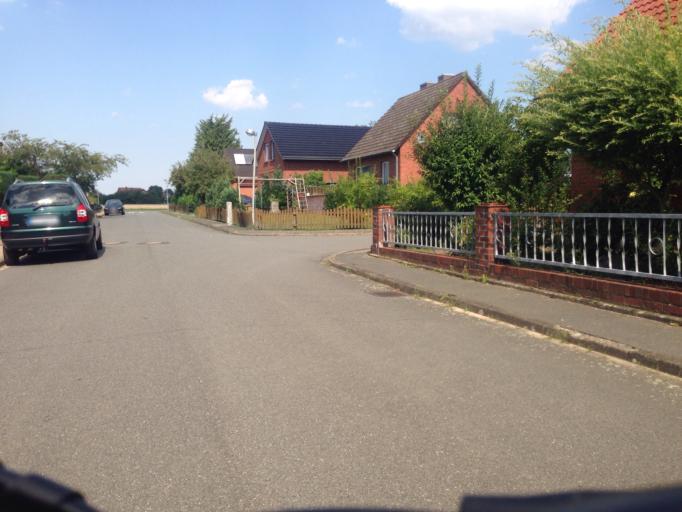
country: DE
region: Lower Saxony
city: Adendorf
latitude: 53.2833
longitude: 10.4379
